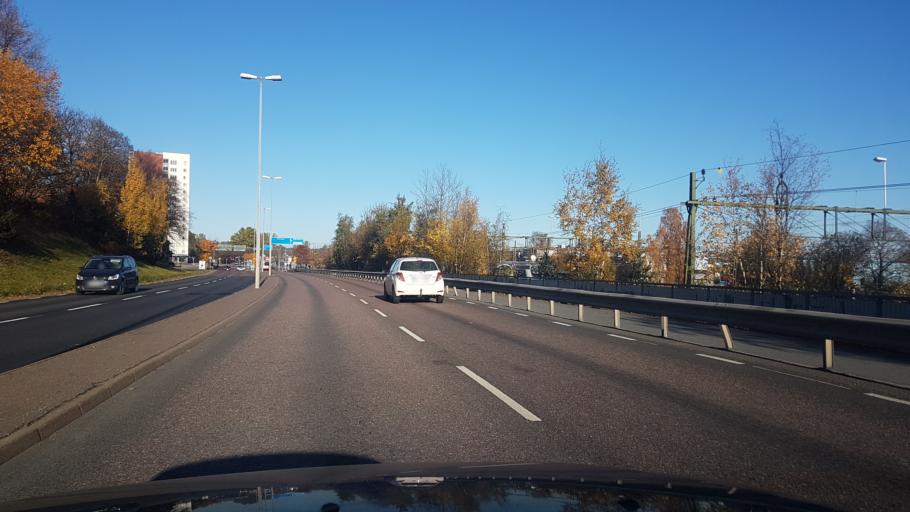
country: SE
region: Stockholm
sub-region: Sigtuna Kommun
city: Marsta
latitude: 59.6255
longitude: 17.8608
